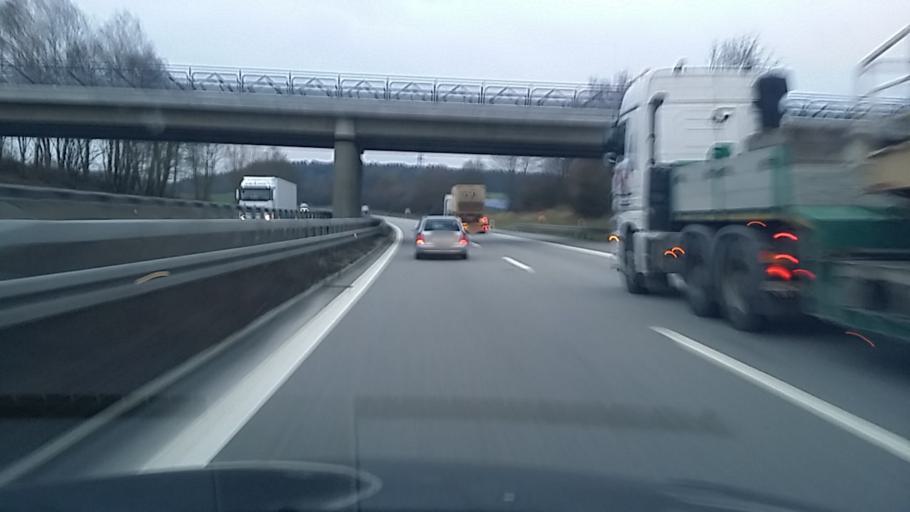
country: DE
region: Bavaria
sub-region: Upper Palatinate
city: Hohenfels
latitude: 49.1616
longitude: 11.8387
